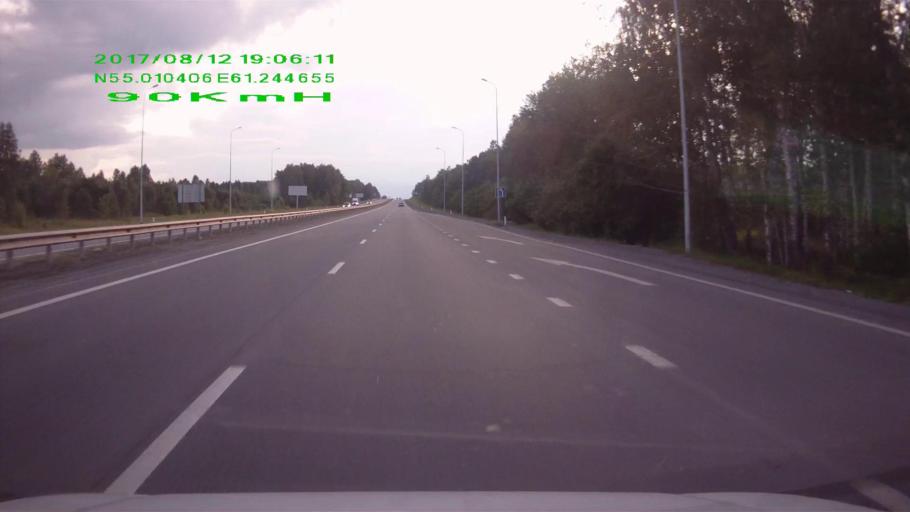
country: RU
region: Chelyabinsk
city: Sargazy
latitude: 55.0092
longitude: 61.2276
